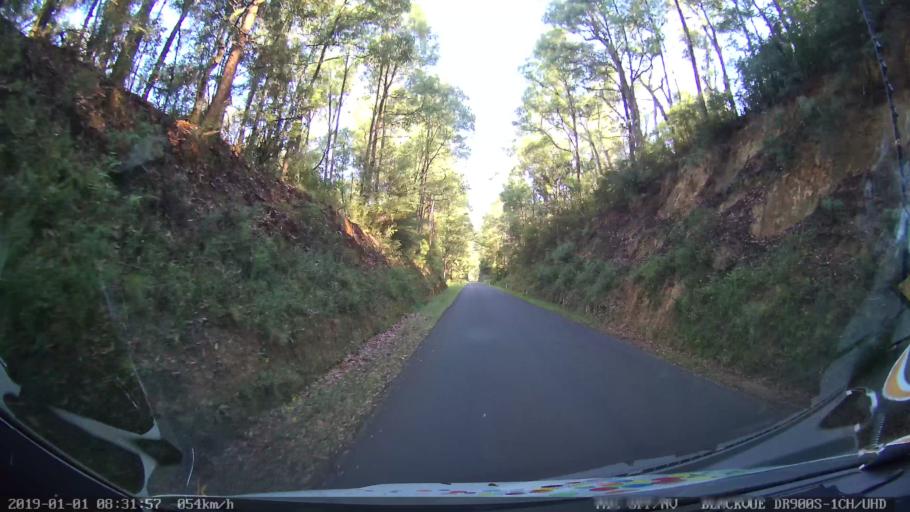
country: AU
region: New South Wales
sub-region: Snowy River
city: Jindabyne
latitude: -36.3660
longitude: 148.2056
